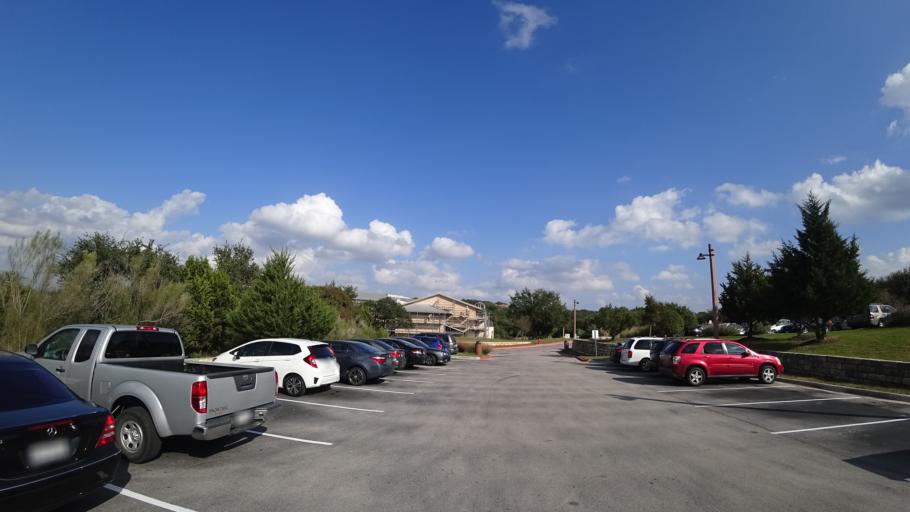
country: US
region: Texas
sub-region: Travis County
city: Barton Creek
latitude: 30.2896
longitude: -97.8703
